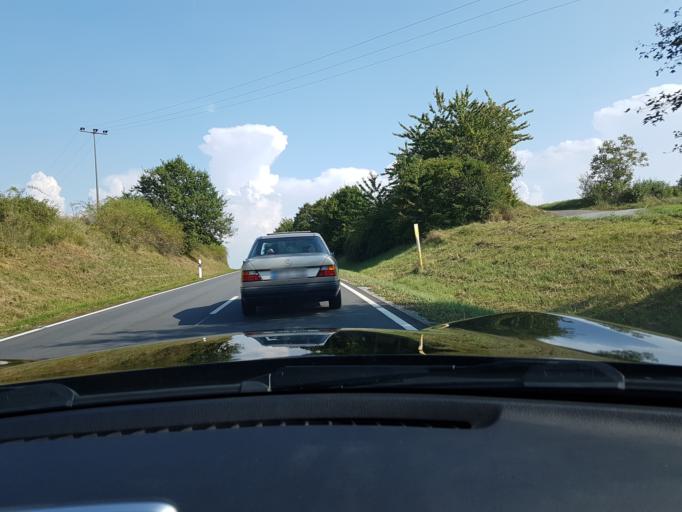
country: DE
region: Baden-Wuerttemberg
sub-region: Karlsruhe Region
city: Seckach
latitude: 49.4772
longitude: 9.3744
